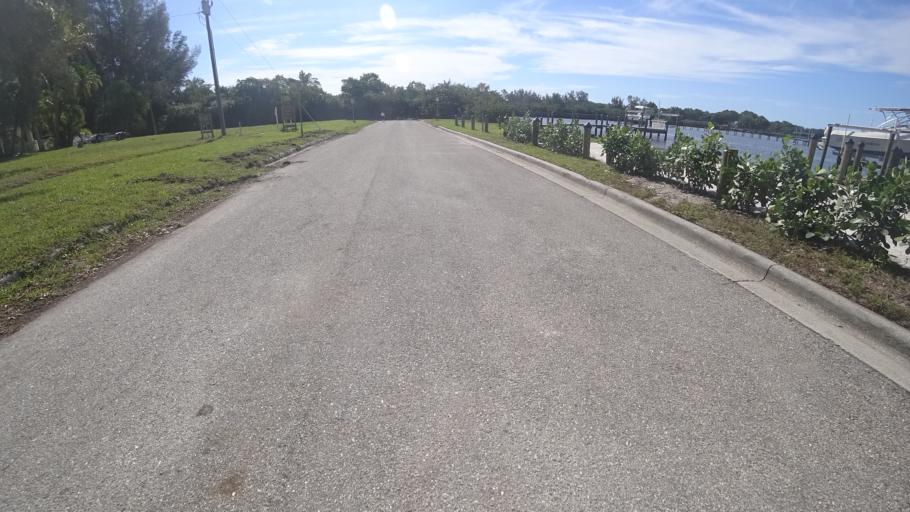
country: US
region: Florida
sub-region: Manatee County
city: West Bradenton
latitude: 27.5029
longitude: -82.6455
